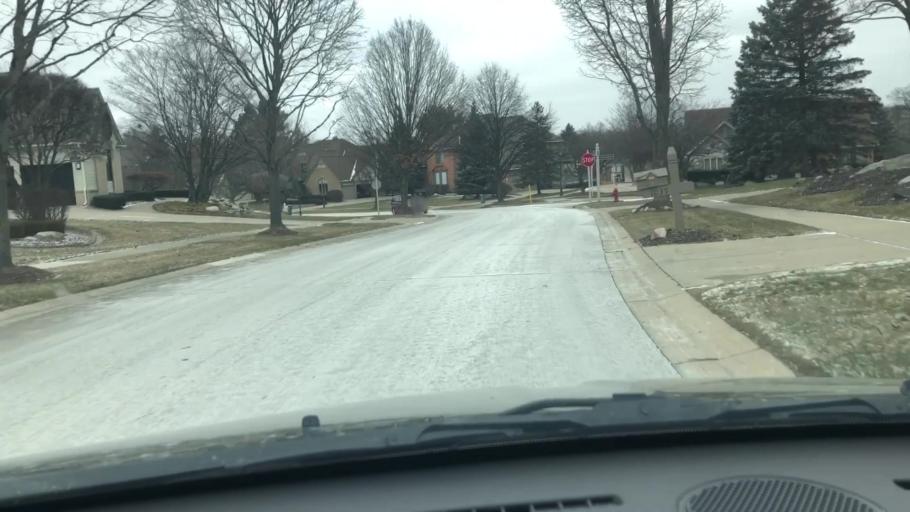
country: US
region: Michigan
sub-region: Oakland County
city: Rochester
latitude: 42.6915
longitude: -83.1152
